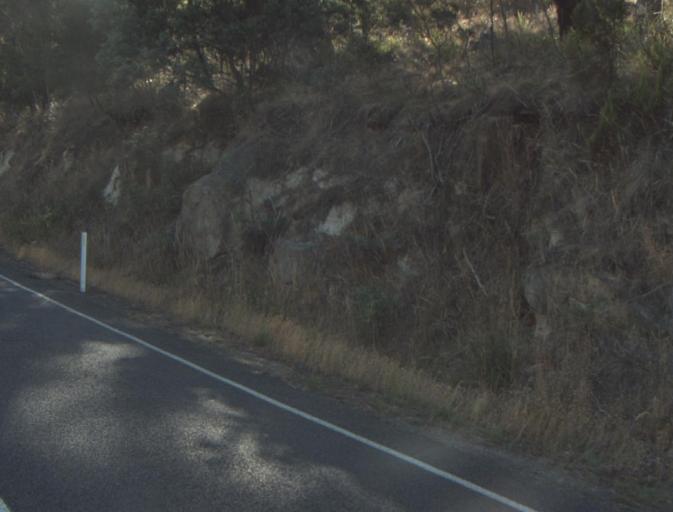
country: AU
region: Tasmania
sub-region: Launceston
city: Newstead
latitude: -41.4202
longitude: 147.2739
